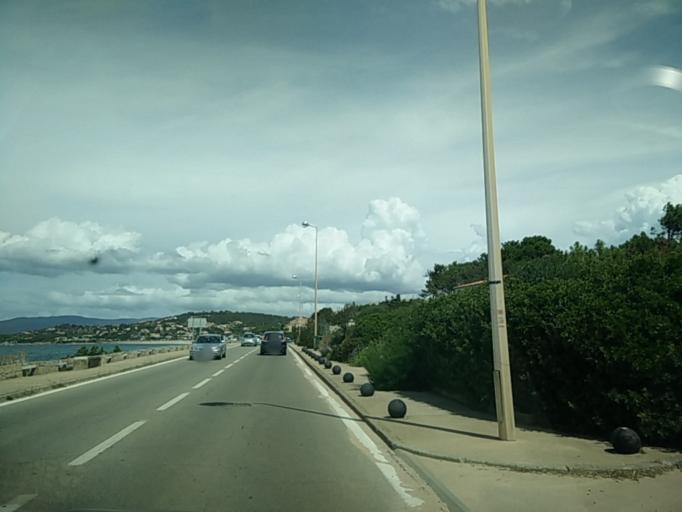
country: FR
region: Corsica
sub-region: Departement de la Corse-du-Sud
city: Pietrosella
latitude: 41.8575
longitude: 8.7913
